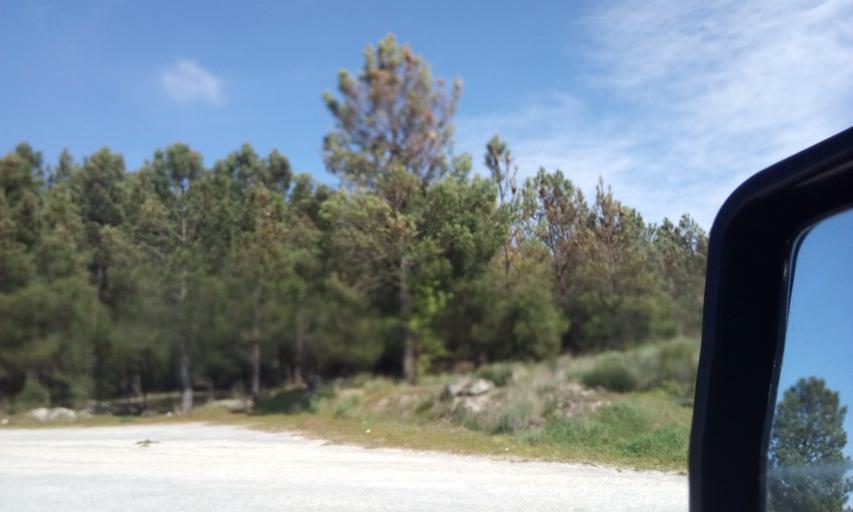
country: PT
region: Guarda
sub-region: Celorico da Beira
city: Celorico da Beira
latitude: 40.6332
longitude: -7.4037
